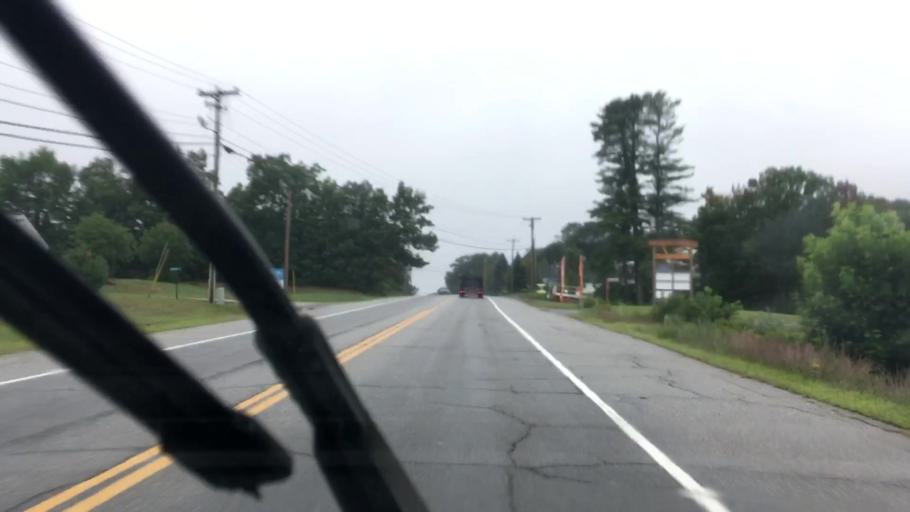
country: US
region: Maine
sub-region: Cumberland County
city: Raymond
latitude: 43.9668
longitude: -70.5829
